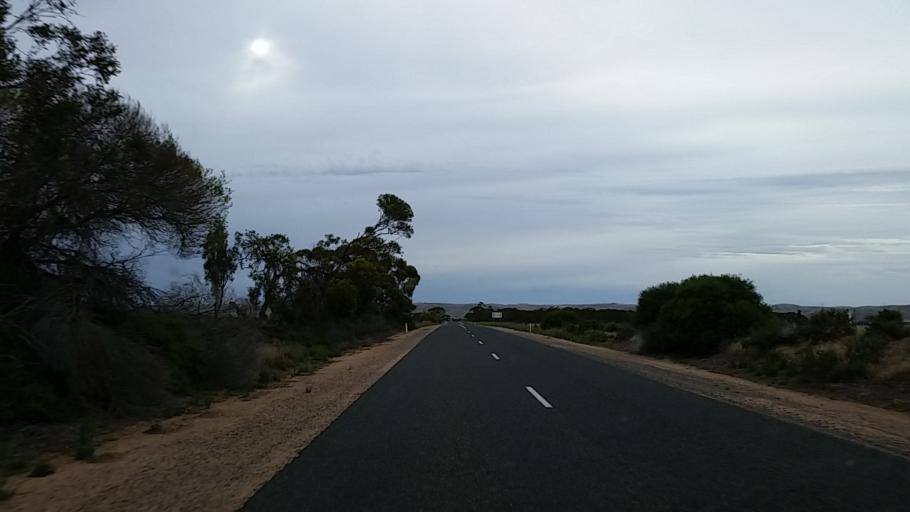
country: AU
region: South Australia
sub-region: Mid Murray
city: Mannum
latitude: -34.7554
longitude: 139.2789
